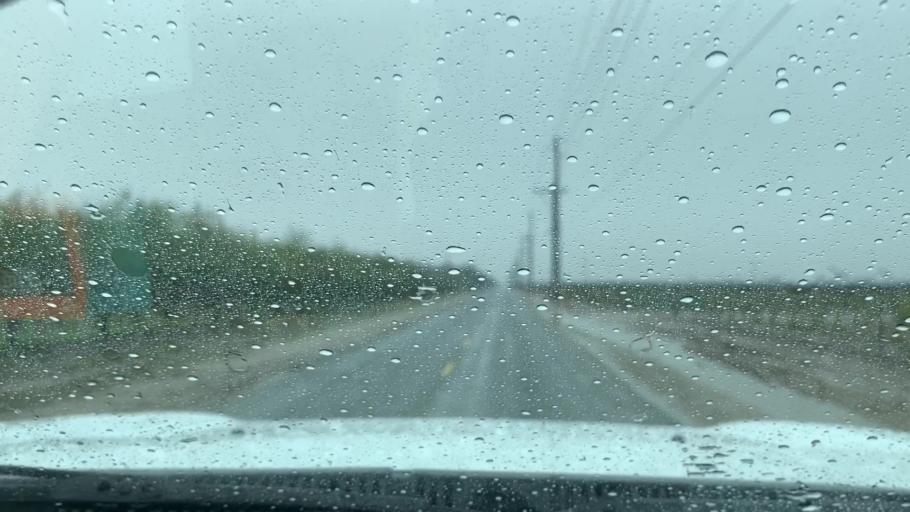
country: US
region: California
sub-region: Tulare County
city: Richgrove
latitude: 35.8341
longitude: -119.1763
